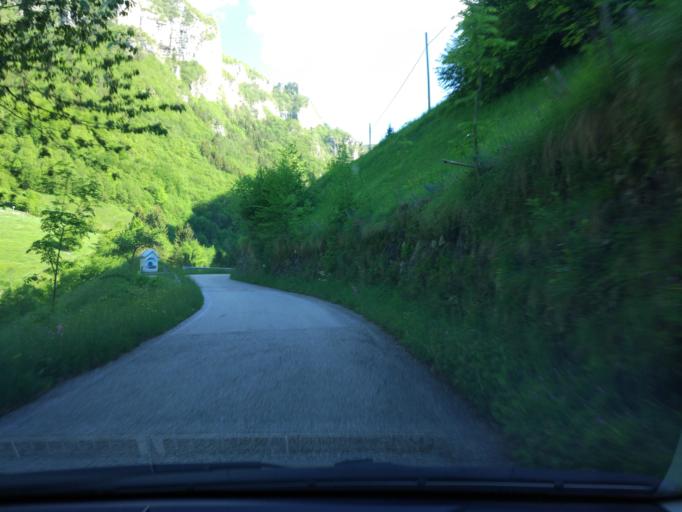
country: IT
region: Veneto
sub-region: Provincia di Verona
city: Selva di Progno
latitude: 45.6608
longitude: 11.1166
